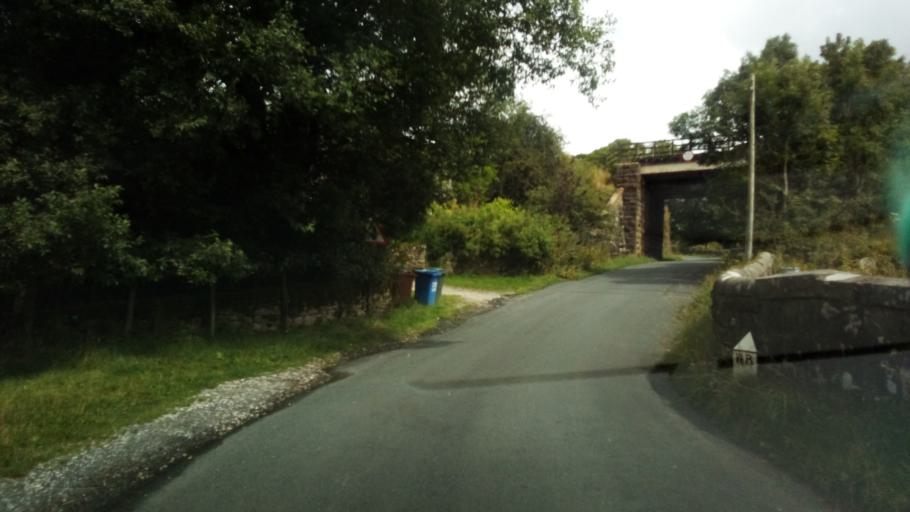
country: GB
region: England
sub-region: North Yorkshire
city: Ingleton
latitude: 54.1046
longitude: -2.4103
